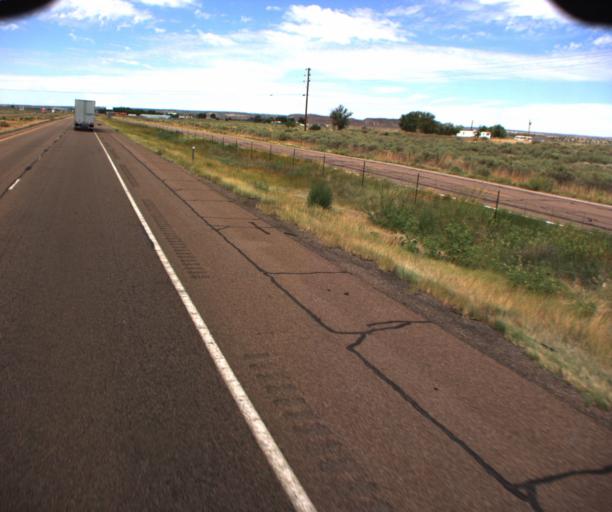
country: US
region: Arizona
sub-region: Apache County
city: Houck
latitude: 35.2030
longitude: -109.3770
